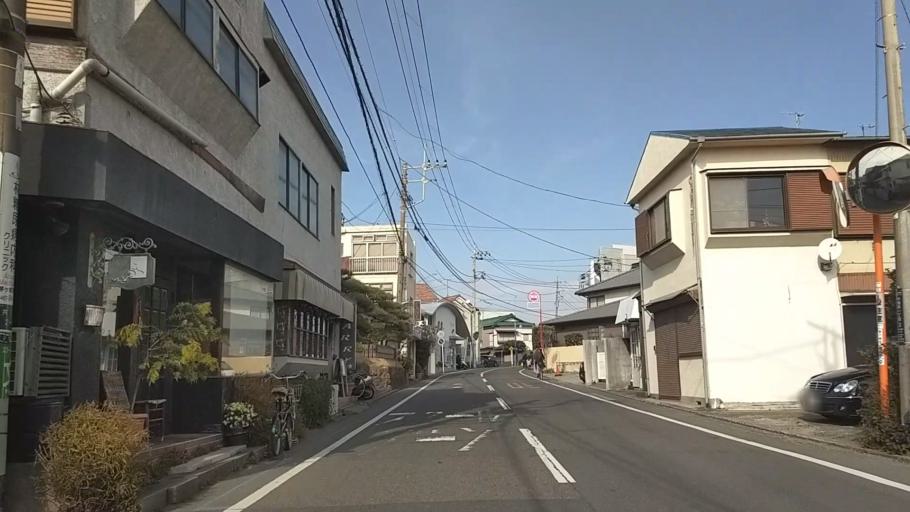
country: JP
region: Kanagawa
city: Chigasaki
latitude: 35.3257
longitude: 139.4025
